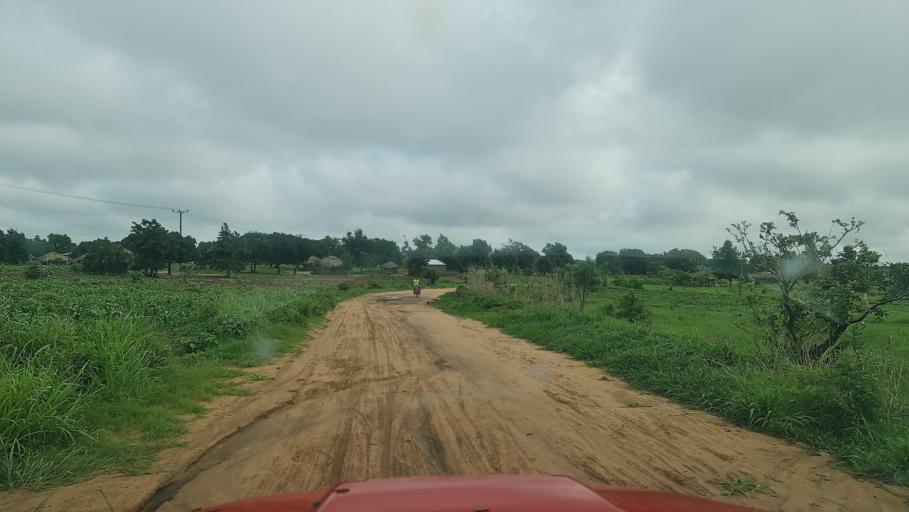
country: MW
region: Southern Region
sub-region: Nsanje District
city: Nsanje
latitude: -17.1940
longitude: 35.7016
